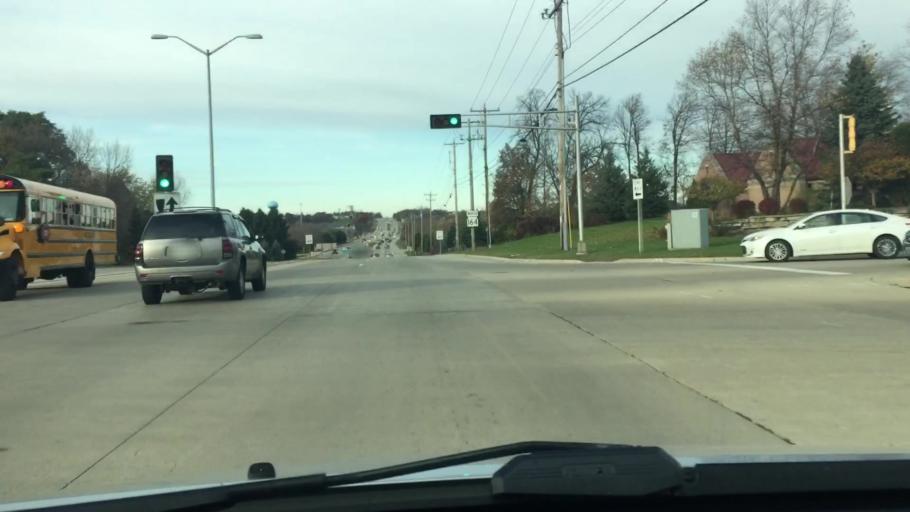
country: US
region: Wisconsin
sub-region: Waukesha County
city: Pewaukee
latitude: 43.0604
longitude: -88.2251
